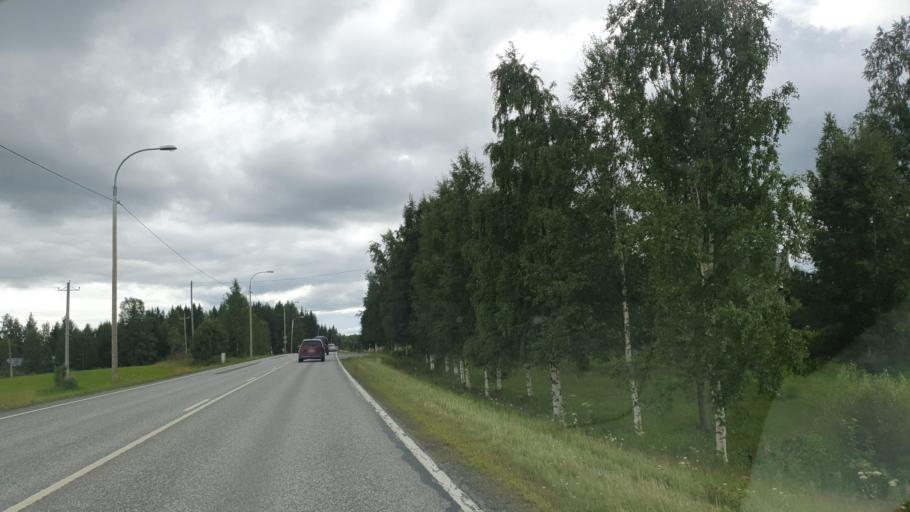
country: FI
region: Northern Savo
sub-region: Ylae-Savo
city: Sonkajaervi
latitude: 63.7273
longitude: 27.3737
